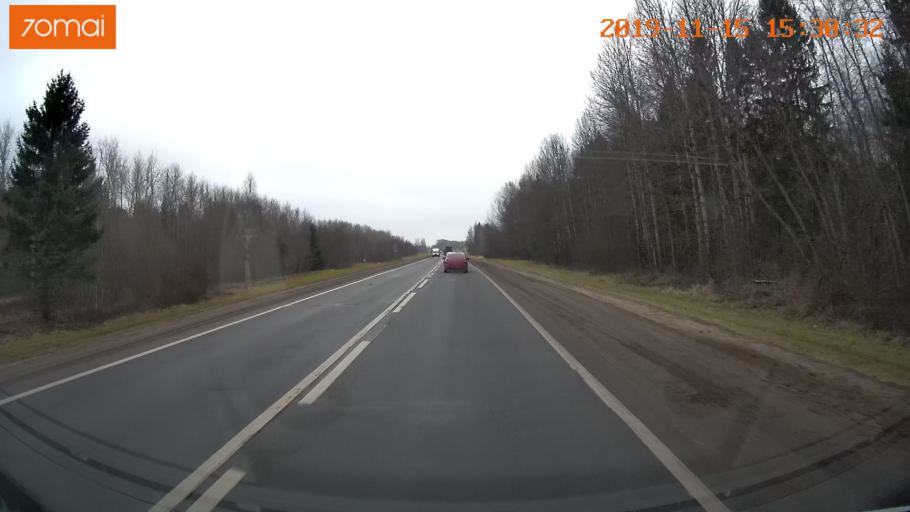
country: RU
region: Jaroslavl
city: Danilov
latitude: 58.1092
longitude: 40.1126
